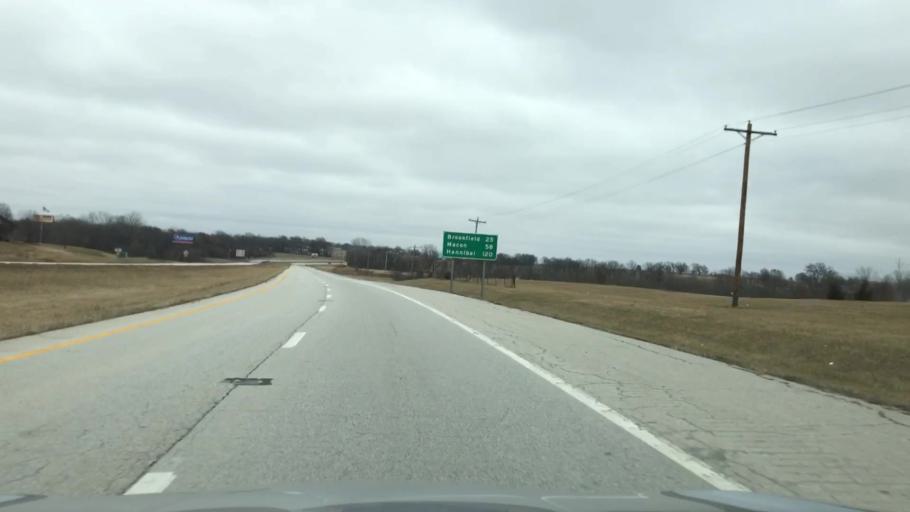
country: US
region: Missouri
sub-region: Livingston County
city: Chillicothe
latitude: 39.7782
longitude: -93.5407
